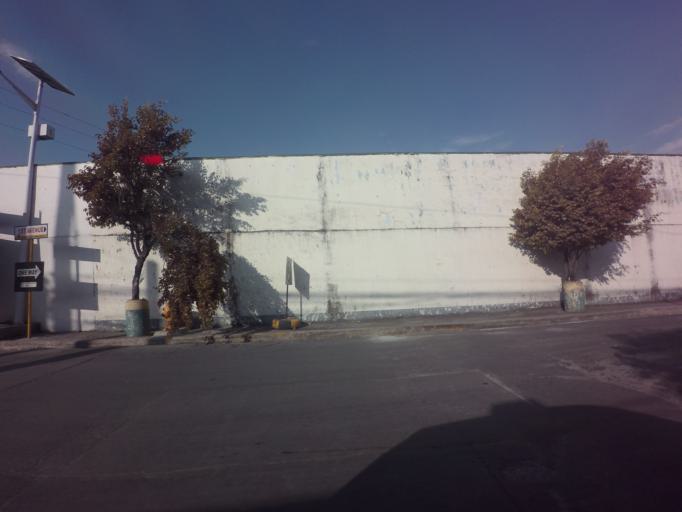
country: PH
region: Calabarzon
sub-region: Province of Rizal
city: Taguig
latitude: 14.4821
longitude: 121.0494
